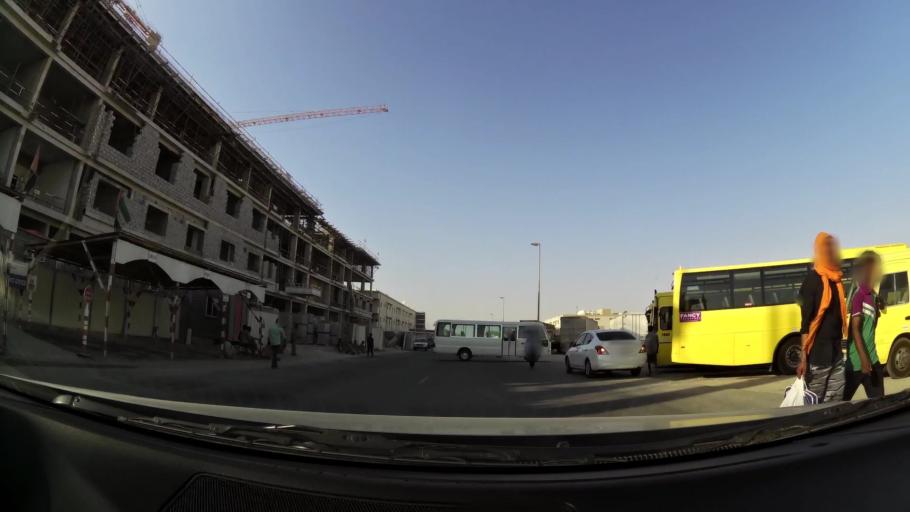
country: AE
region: Dubai
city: Dubai
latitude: 25.1297
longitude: 55.2384
